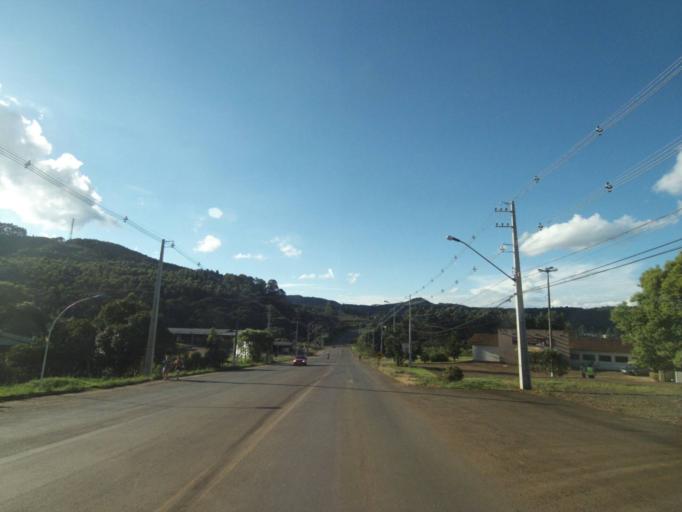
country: BR
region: Parana
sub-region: Uniao Da Vitoria
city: Uniao da Vitoria
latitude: -26.1606
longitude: -51.5388
